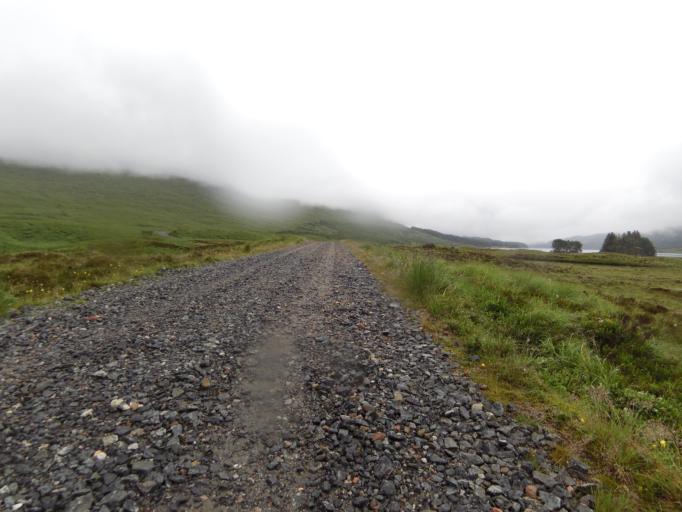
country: GB
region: Scotland
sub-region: Highland
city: Spean Bridge
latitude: 56.7666
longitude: -4.6738
